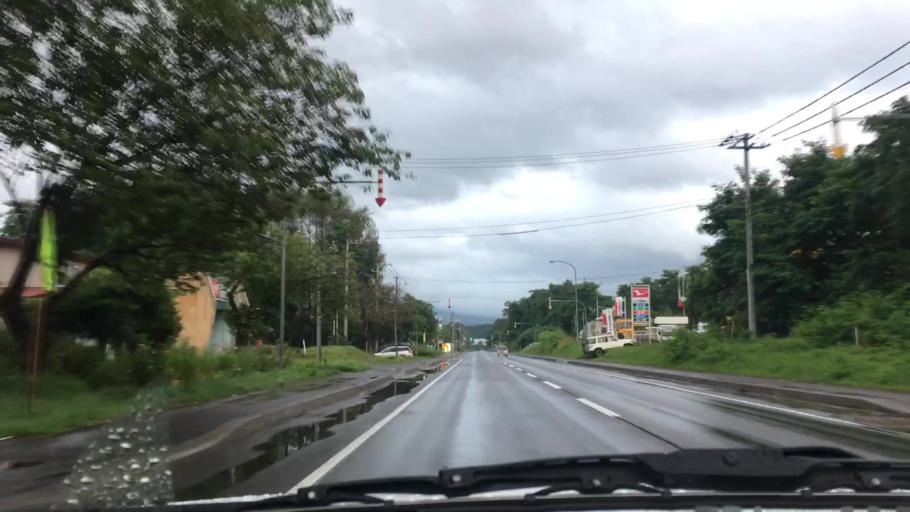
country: JP
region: Hokkaido
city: Nanae
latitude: 42.1094
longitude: 140.5524
